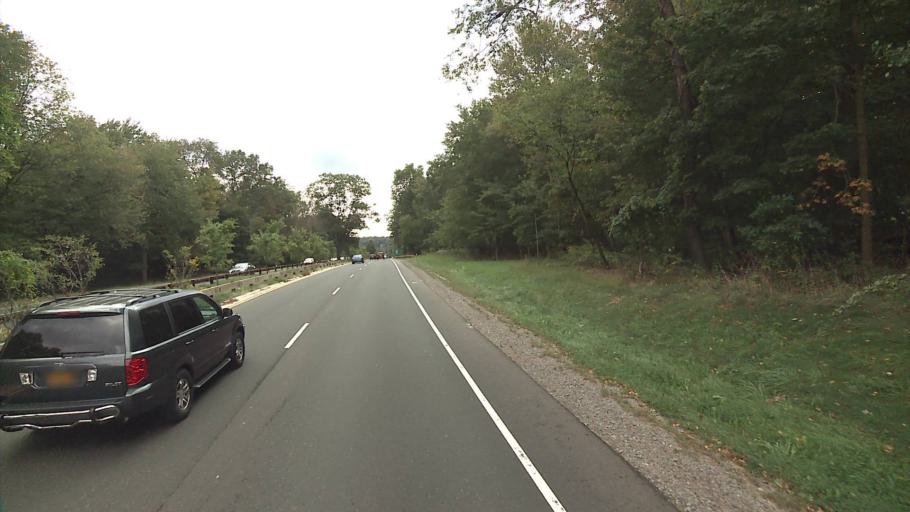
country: US
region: Connecticut
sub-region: Fairfield County
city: New Canaan
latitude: 41.1188
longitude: -73.5142
